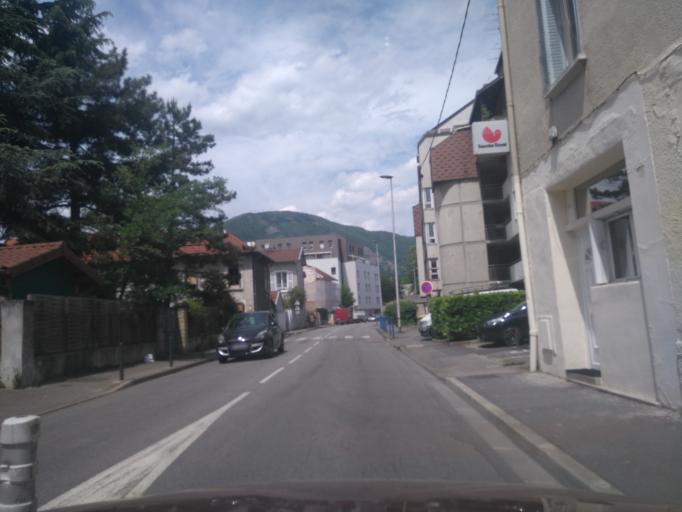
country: FR
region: Rhone-Alpes
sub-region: Departement de l'Isere
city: La Tronche
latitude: 45.1840
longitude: 5.7475
